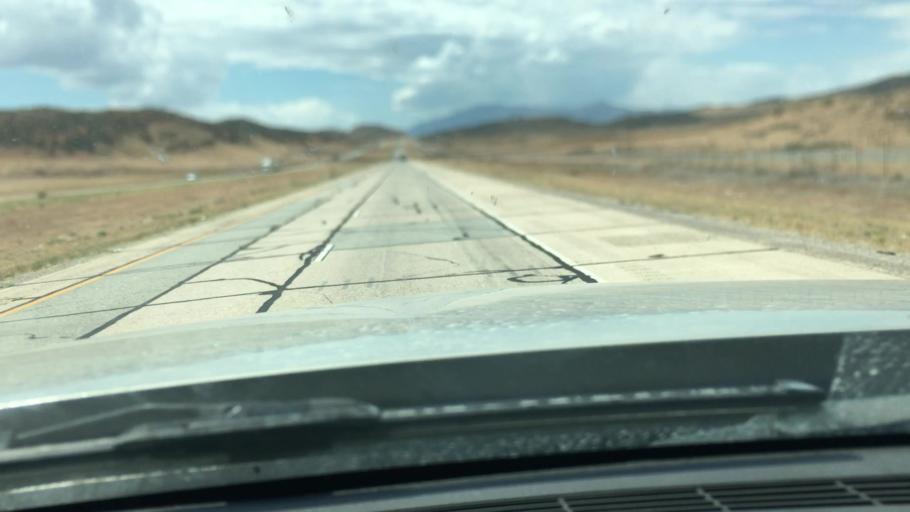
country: US
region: Utah
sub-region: Sanpete County
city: Gunnison
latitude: 39.3687
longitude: -112.0800
